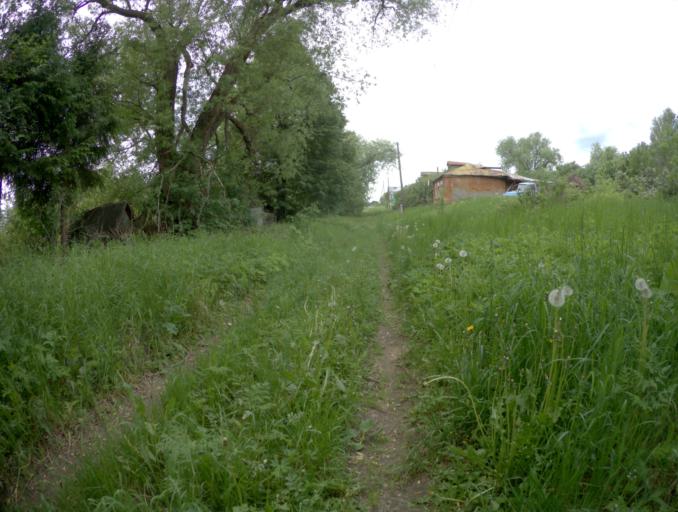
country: RU
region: Vladimir
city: Stavrovo
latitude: 56.2368
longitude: 39.9282
